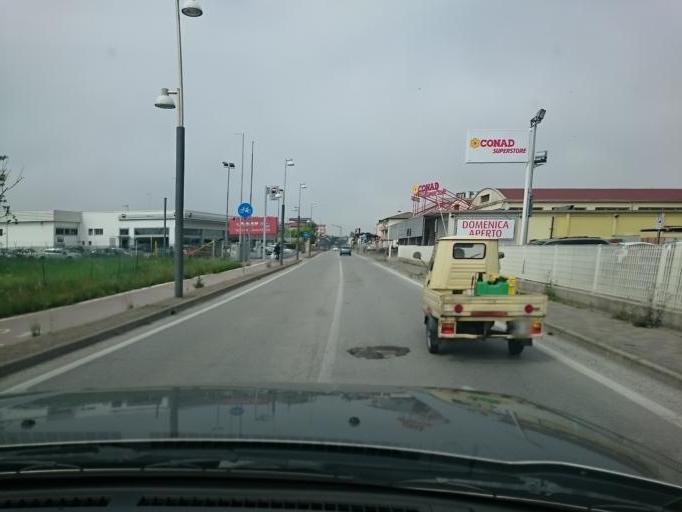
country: IT
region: Veneto
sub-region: Provincia di Venezia
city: Chioggia
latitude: 45.1930
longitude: 12.2816
